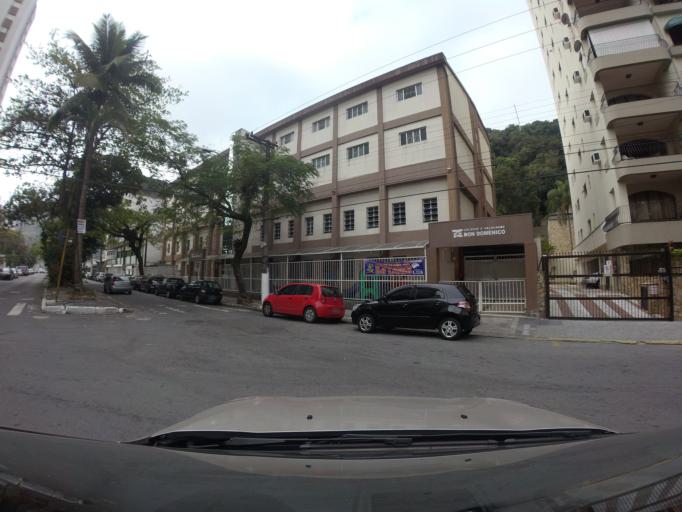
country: BR
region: Sao Paulo
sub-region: Guaruja
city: Guaruja
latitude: -23.9932
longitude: -46.2539
